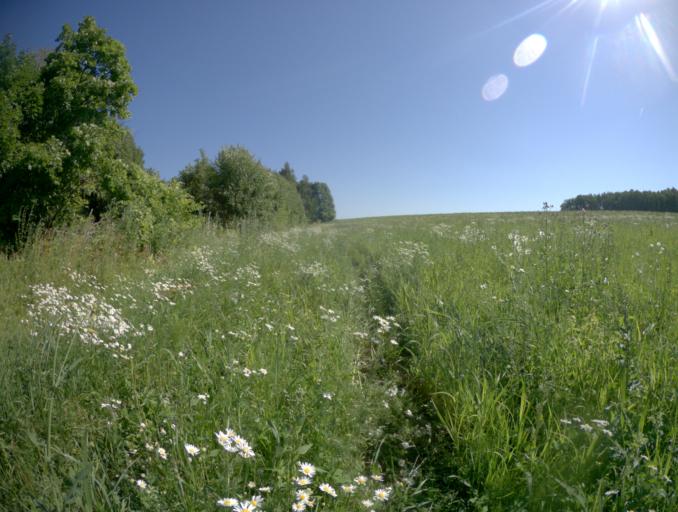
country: RU
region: Nizjnij Novgorod
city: Reshetikha
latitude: 56.1743
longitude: 43.3629
